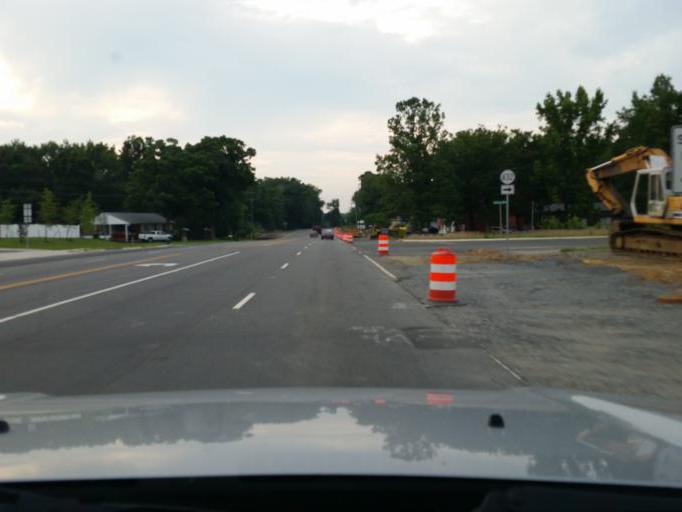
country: US
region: Virginia
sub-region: Spotsylvania County
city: Spotsylvania Courthouse
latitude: 38.1356
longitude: -77.5218
